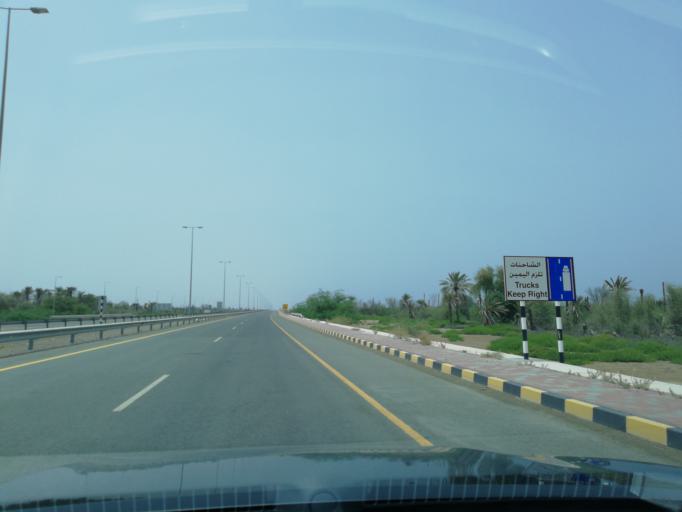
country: OM
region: Al Batinah
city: Shinas
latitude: 24.6434
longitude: 56.5192
